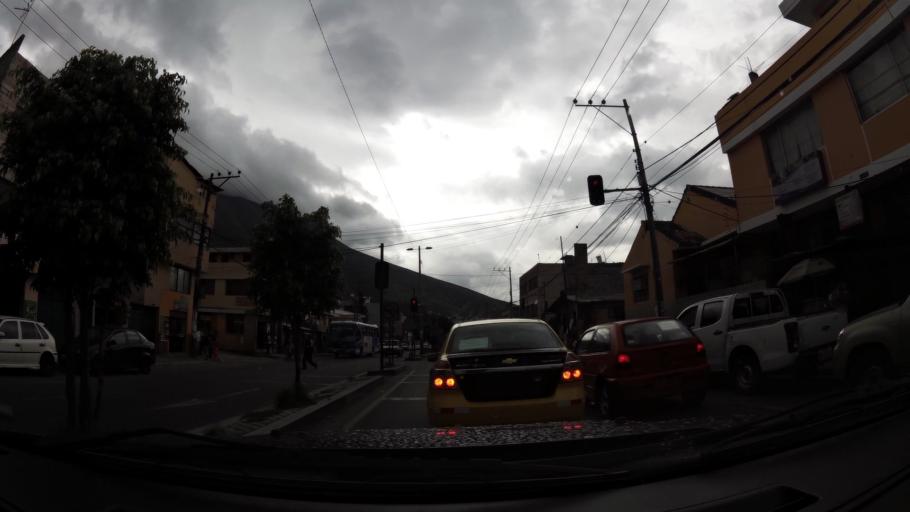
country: EC
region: Pichincha
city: Quito
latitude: -0.0558
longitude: -78.4550
